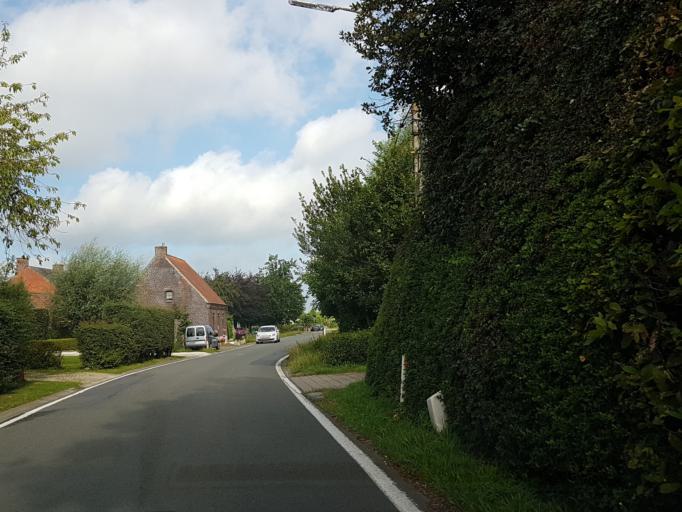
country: BE
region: Flanders
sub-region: Provincie Oost-Vlaanderen
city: Sint-Martens-Latem
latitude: 51.0561
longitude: 3.6454
